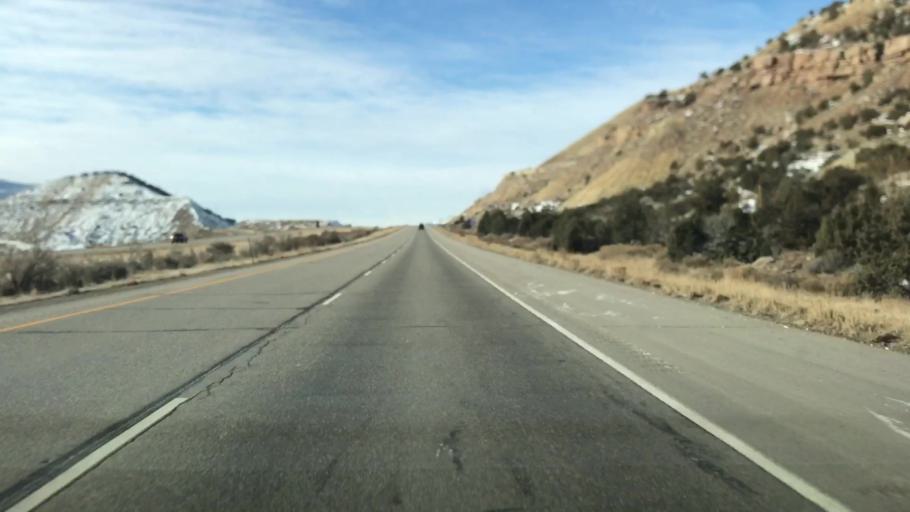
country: US
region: Colorado
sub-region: Garfield County
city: Rifle
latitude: 39.5110
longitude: -107.8743
